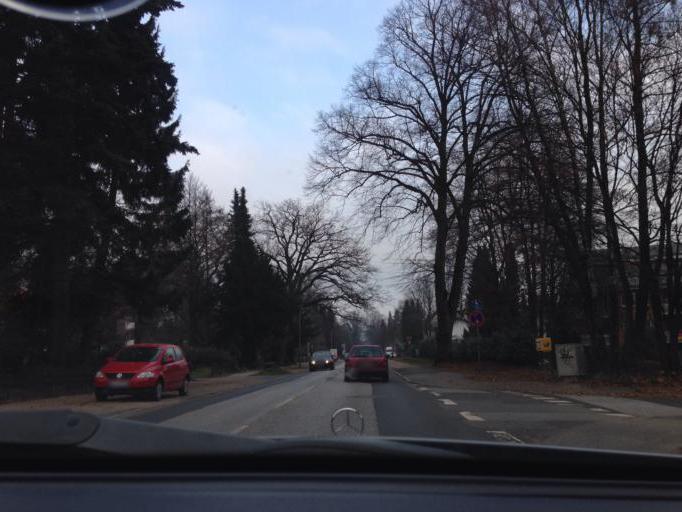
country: DE
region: Hamburg
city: Farmsen-Berne
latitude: 53.6172
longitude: 10.1588
